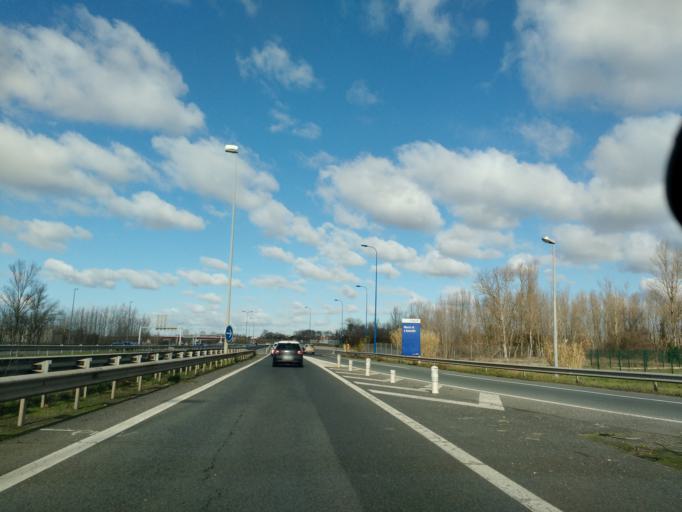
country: FR
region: Midi-Pyrenees
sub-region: Departement de la Haute-Garonne
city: Ramonville-Saint-Agne
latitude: 43.5593
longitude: 1.4901
